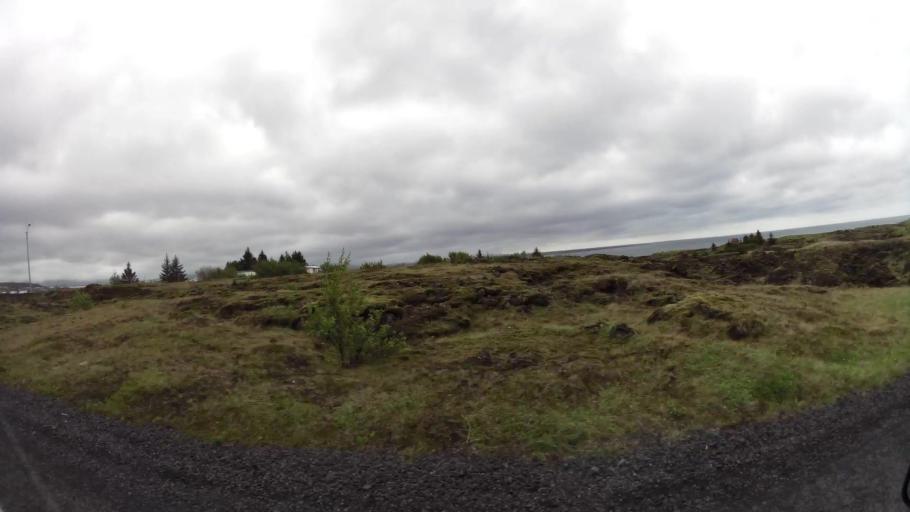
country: IS
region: Capital Region
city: Hafnarfjoerdur
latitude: 64.0800
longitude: -21.9778
